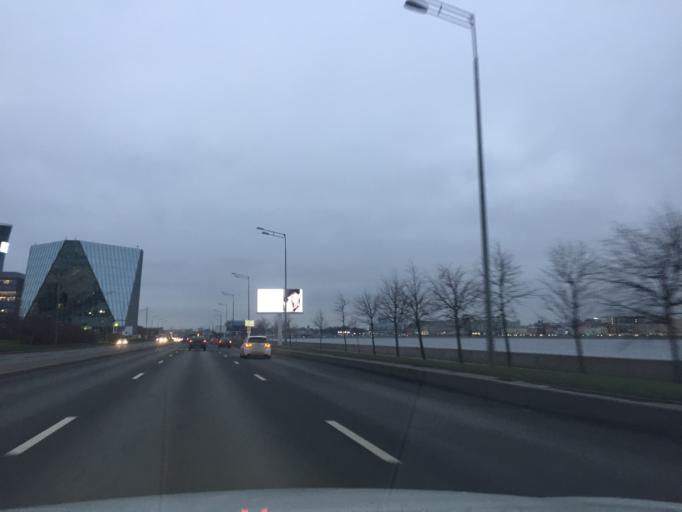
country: RU
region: St.-Petersburg
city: Centralniy
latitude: 59.9366
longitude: 30.4026
